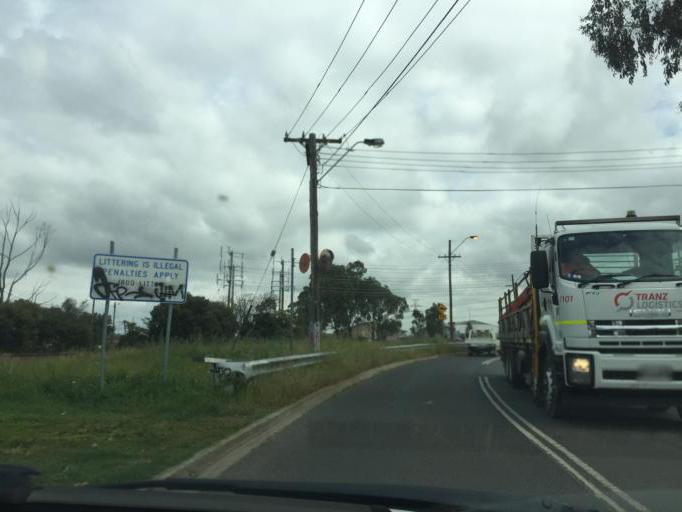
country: AU
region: Victoria
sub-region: Hobsons Bay
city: South Kingsville
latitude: -37.8259
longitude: 144.8699
